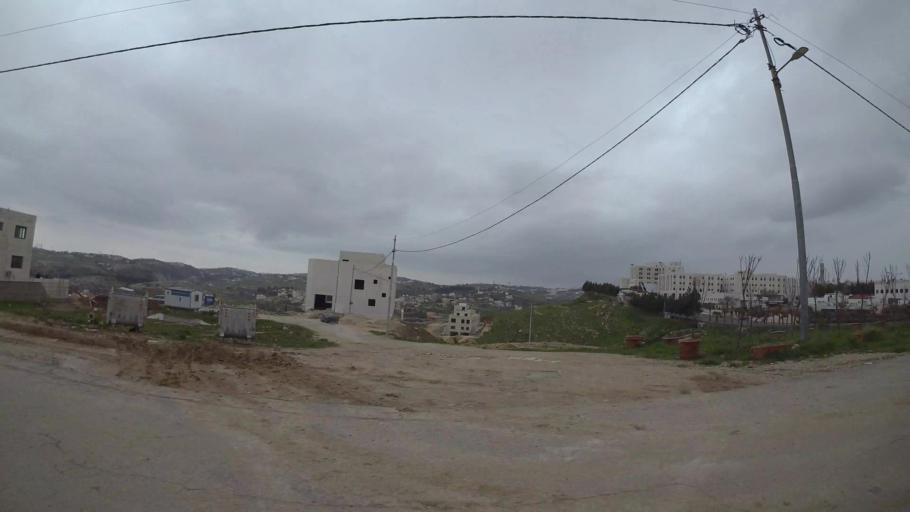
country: JO
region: Amman
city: Wadi as Sir
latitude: 31.9676
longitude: 35.8248
